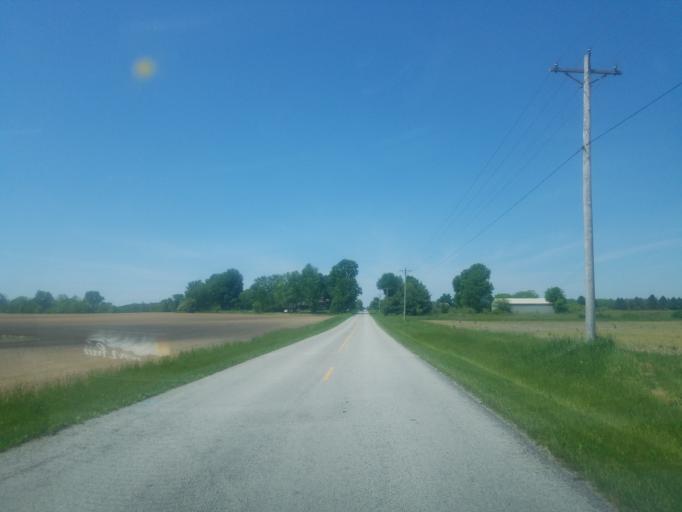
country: US
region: Ohio
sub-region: Huron County
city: New London
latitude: 41.1160
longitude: -82.3670
